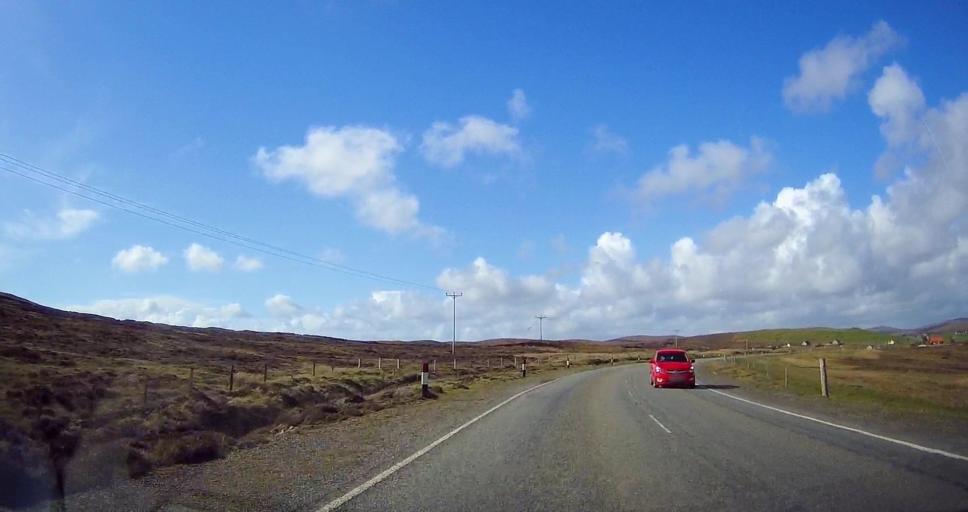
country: GB
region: Scotland
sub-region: Shetland Islands
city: Lerwick
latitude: 60.2284
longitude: -1.2370
